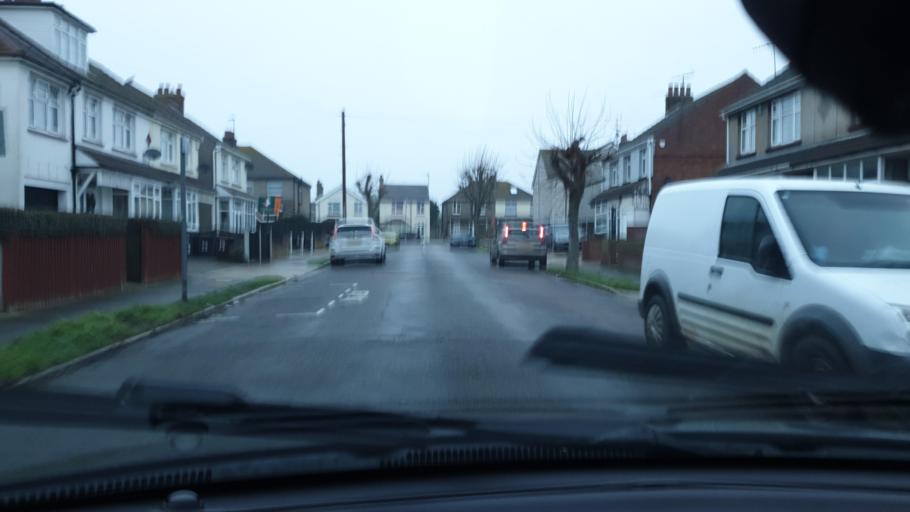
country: GB
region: England
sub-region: Essex
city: Clacton-on-Sea
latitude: 51.7911
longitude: 1.1441
